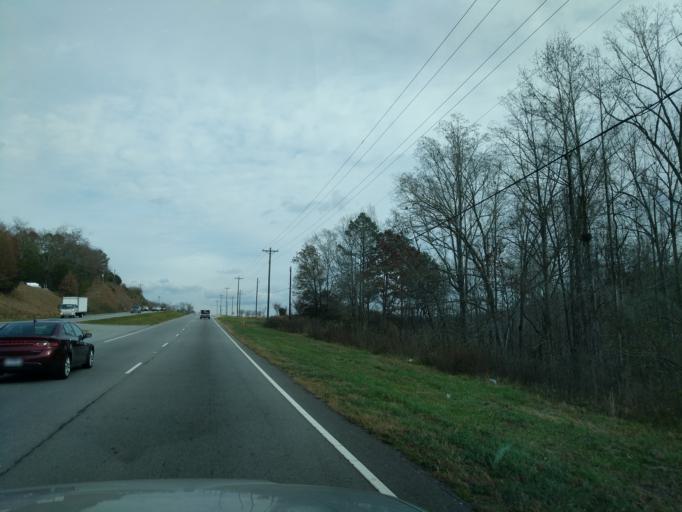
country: US
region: South Carolina
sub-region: Oconee County
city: Utica
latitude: 34.7014
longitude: -82.9188
